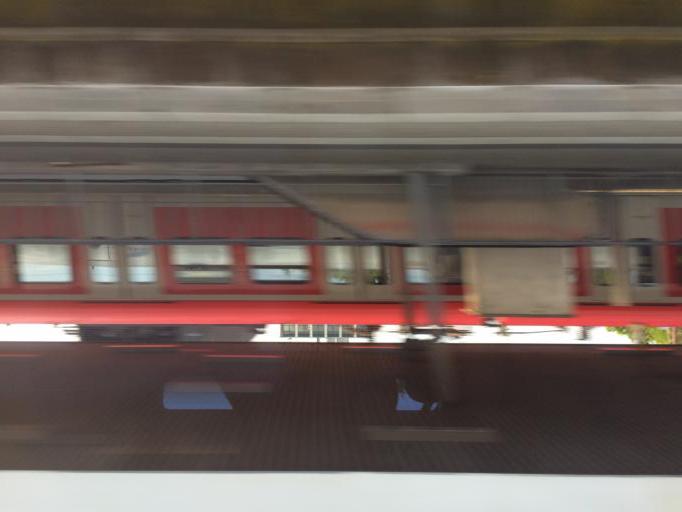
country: DE
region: North Rhine-Westphalia
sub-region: Regierungsbezirk Dusseldorf
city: Essen
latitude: 51.4546
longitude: 6.9801
